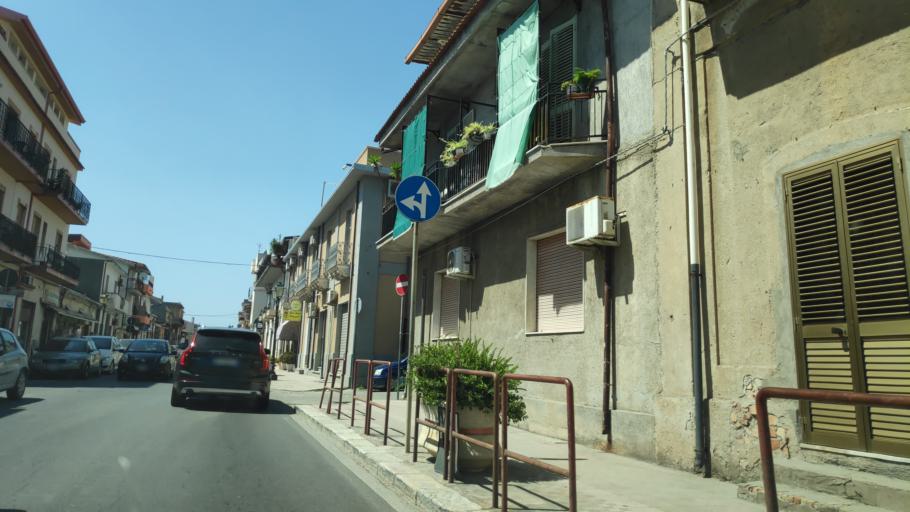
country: IT
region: Calabria
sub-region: Provincia di Reggio Calabria
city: Brancaleone
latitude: 37.9647
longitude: 16.1022
